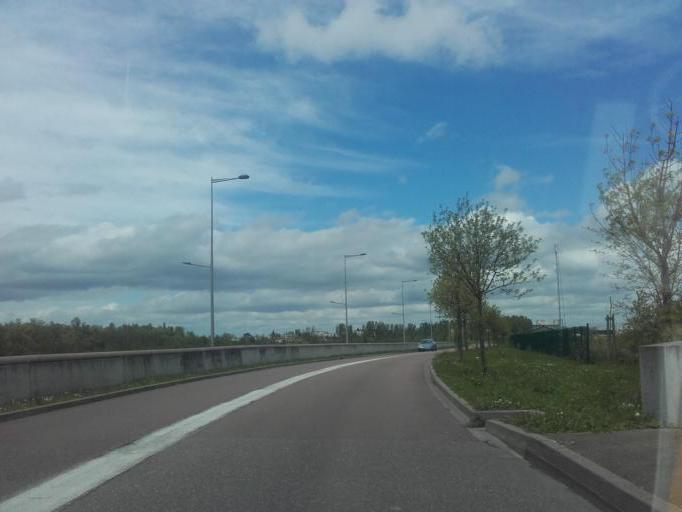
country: FR
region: Bourgogne
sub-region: Departement de Saone-et-Loire
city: Saint-Remy
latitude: 46.7681
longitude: 4.8392
